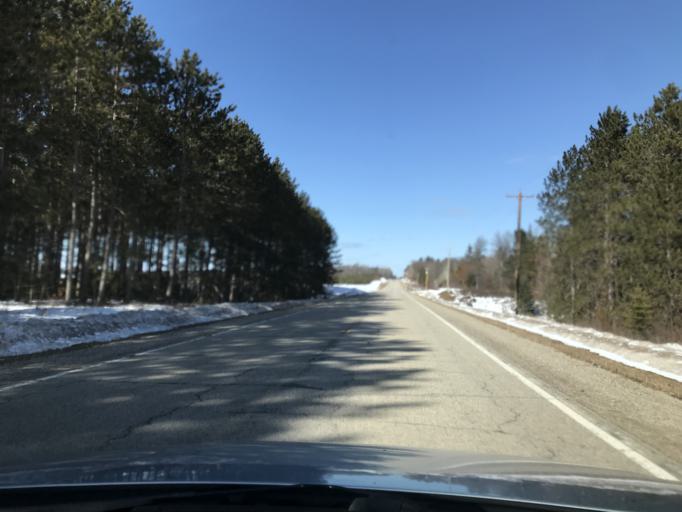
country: US
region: Wisconsin
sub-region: Marinette County
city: Niagara
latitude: 45.3464
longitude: -88.1014
